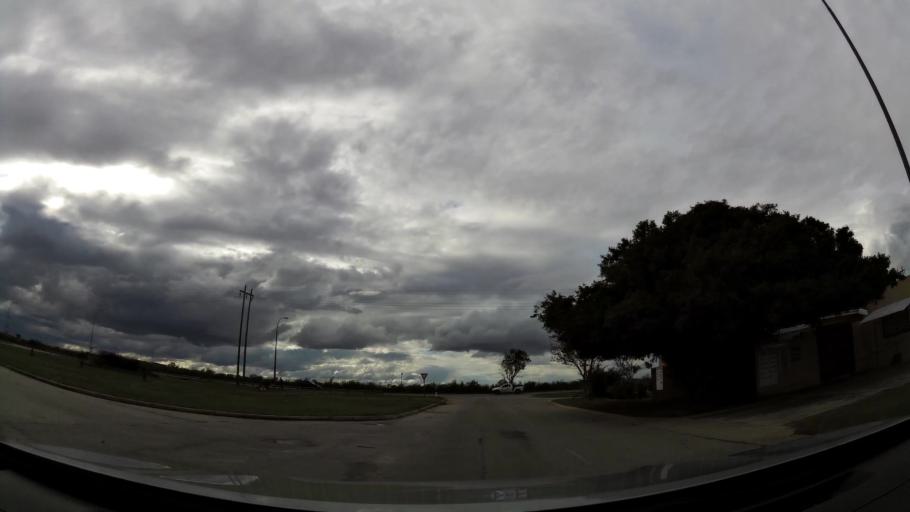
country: ZA
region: Eastern Cape
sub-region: Nelson Mandela Bay Metropolitan Municipality
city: Port Elizabeth
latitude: -33.9362
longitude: 25.4740
